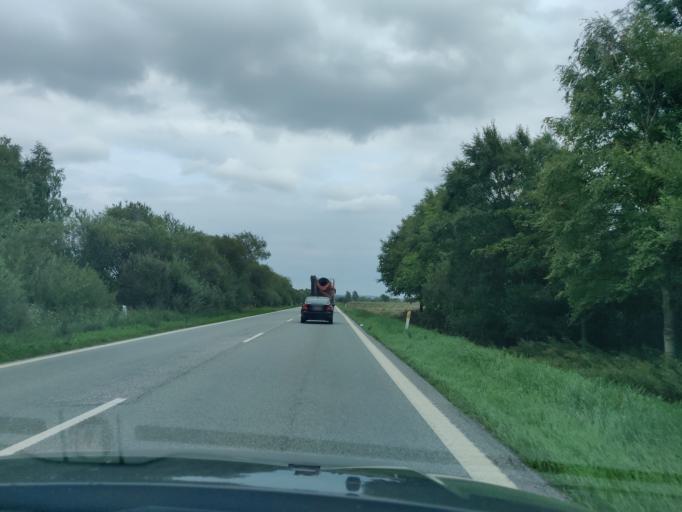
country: DK
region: North Denmark
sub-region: Alborg Kommune
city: Frejlev
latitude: 57.0141
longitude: 9.8196
